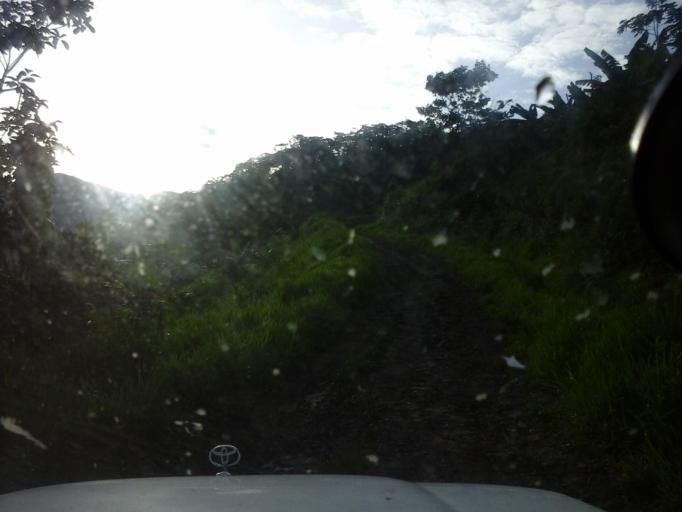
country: CO
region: Cesar
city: Agustin Codazzi
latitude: 10.1519
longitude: -73.1217
